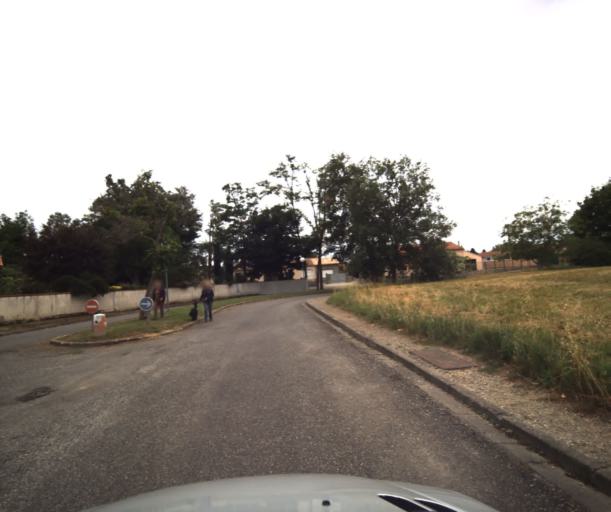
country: FR
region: Midi-Pyrenees
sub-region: Departement de la Haute-Garonne
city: Labarthe-sur-Leze
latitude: 43.4540
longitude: 1.4079
